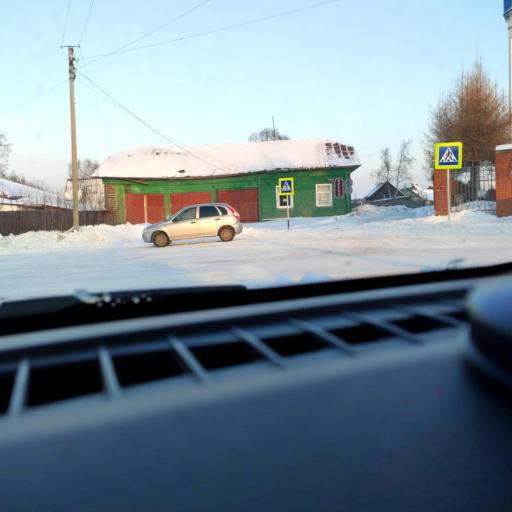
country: RU
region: Perm
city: Orda
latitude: 57.1976
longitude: 56.9007
